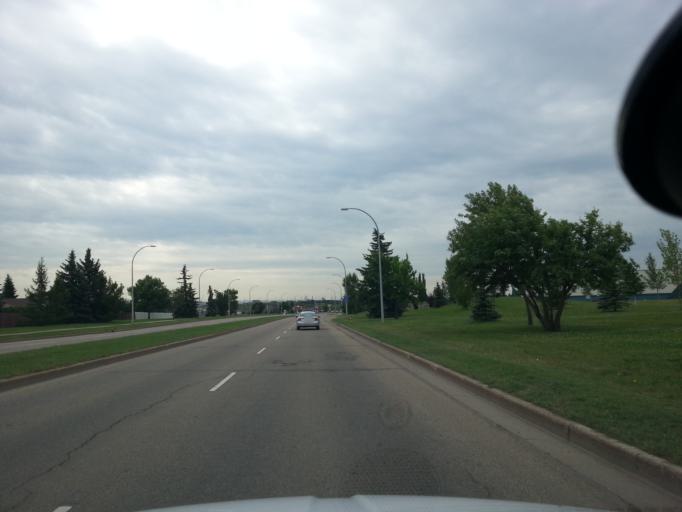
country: CA
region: Alberta
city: Edmonton
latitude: 53.5830
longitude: -113.3835
